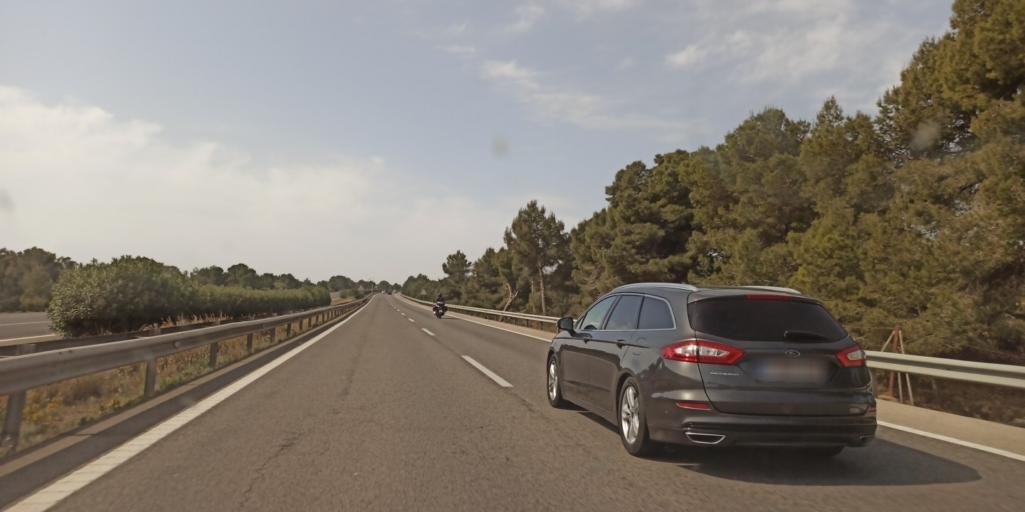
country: ES
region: Catalonia
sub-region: Provincia de Tarragona
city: l'Ametlla de Mar
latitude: 40.8572
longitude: 0.7657
